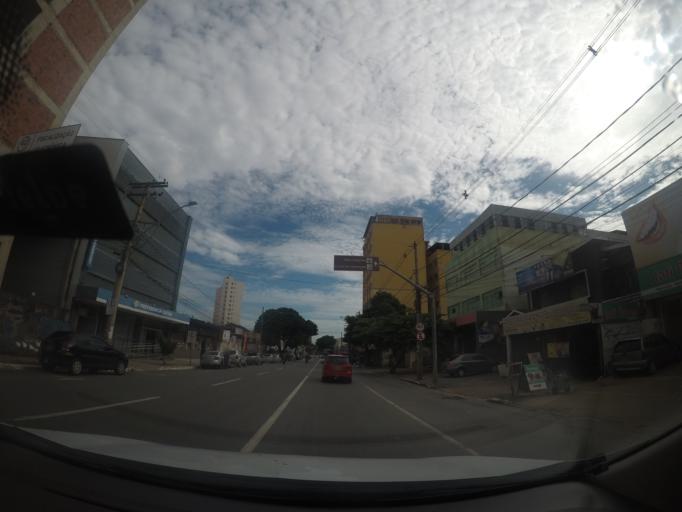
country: BR
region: Goias
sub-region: Goiania
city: Goiania
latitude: -16.6765
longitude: -49.2554
